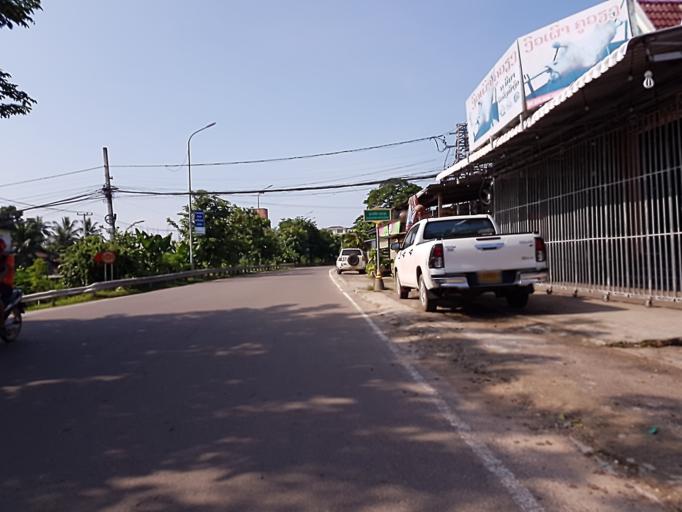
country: LA
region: Vientiane
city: Vientiane
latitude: 17.9473
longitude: 102.6225
